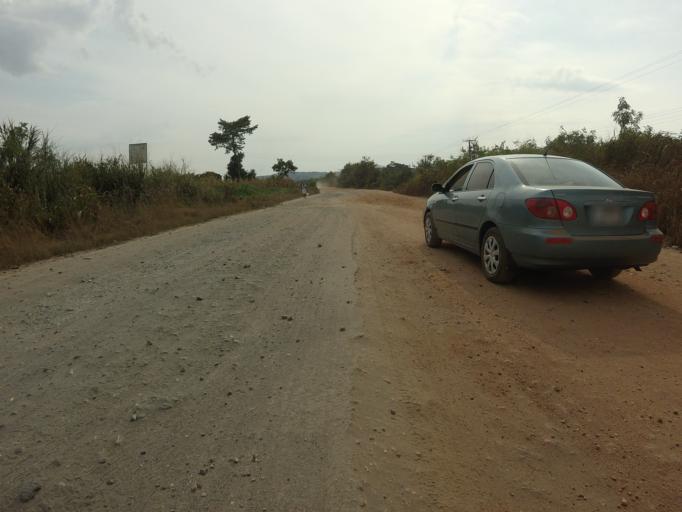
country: GH
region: Volta
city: Ho
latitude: 6.6789
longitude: 0.3183
